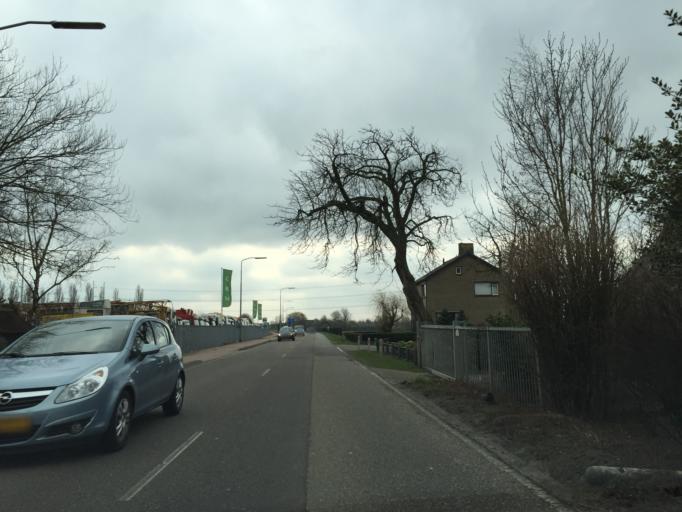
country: NL
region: South Holland
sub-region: Gemeente Zoetermeer
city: Zoetermeer
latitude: 52.0364
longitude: 4.4738
